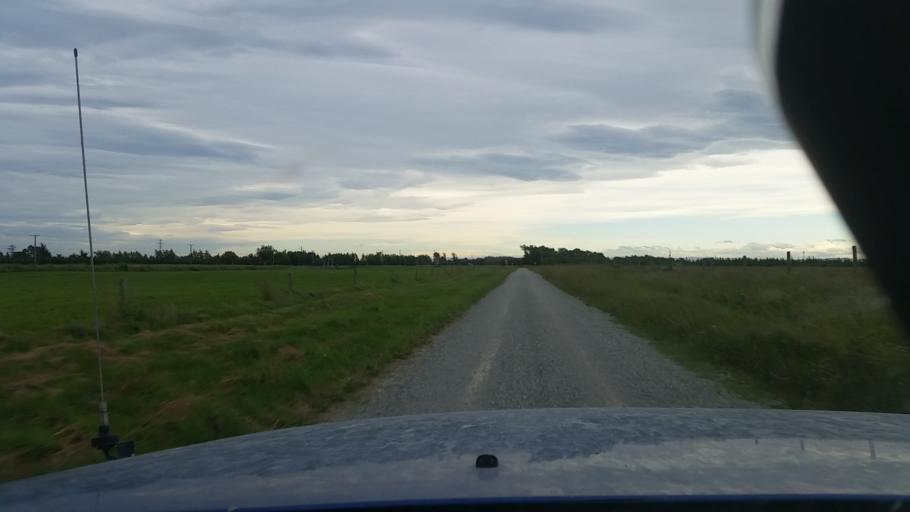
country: NZ
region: Canterbury
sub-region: Ashburton District
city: Tinwald
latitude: -44.0076
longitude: 171.5573
